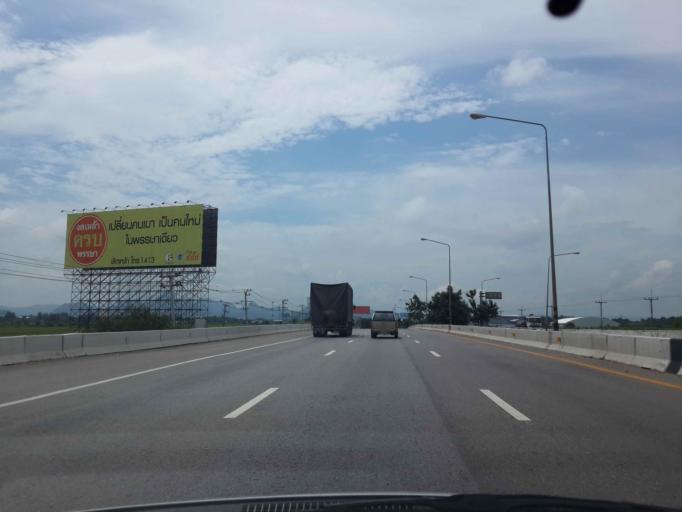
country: TH
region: Ratchaburi
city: Pak Tho
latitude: 13.3414
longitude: 99.8484
